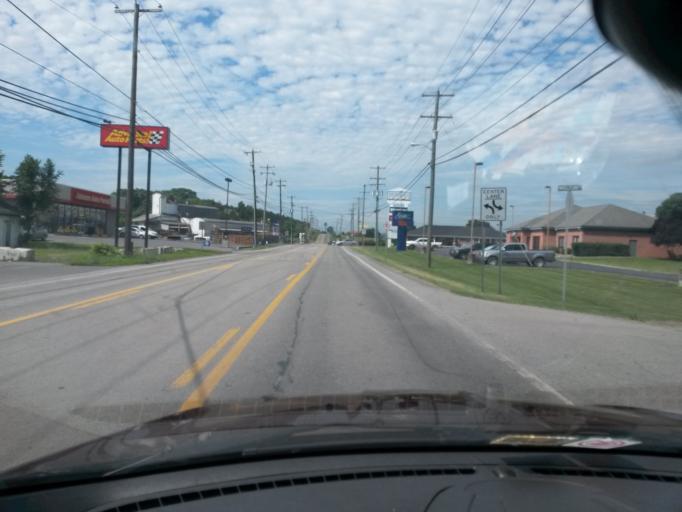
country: US
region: West Virginia
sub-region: Hardy County
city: Moorefield
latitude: 39.0518
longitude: -78.9746
